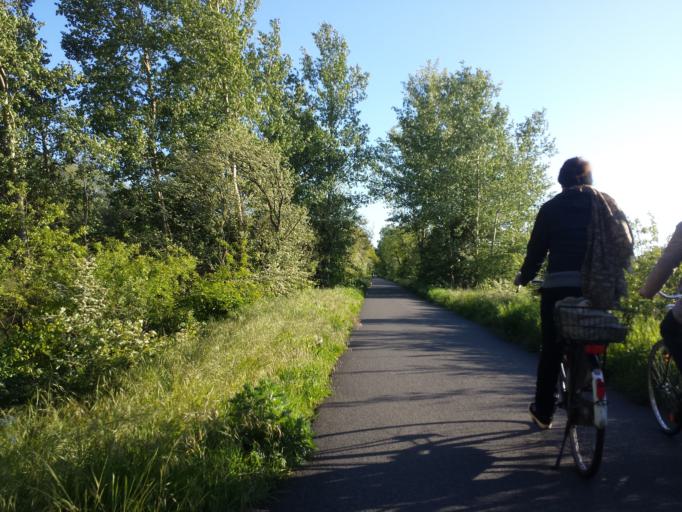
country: DE
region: Lower Saxony
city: Lilienthal
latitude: 53.1117
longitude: 8.8743
